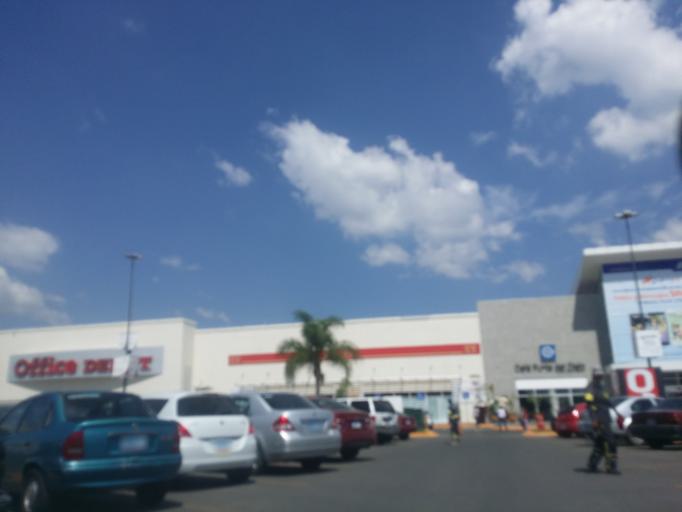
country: MX
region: Guanajuato
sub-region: Leon
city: Medina
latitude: 21.1471
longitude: -101.6487
